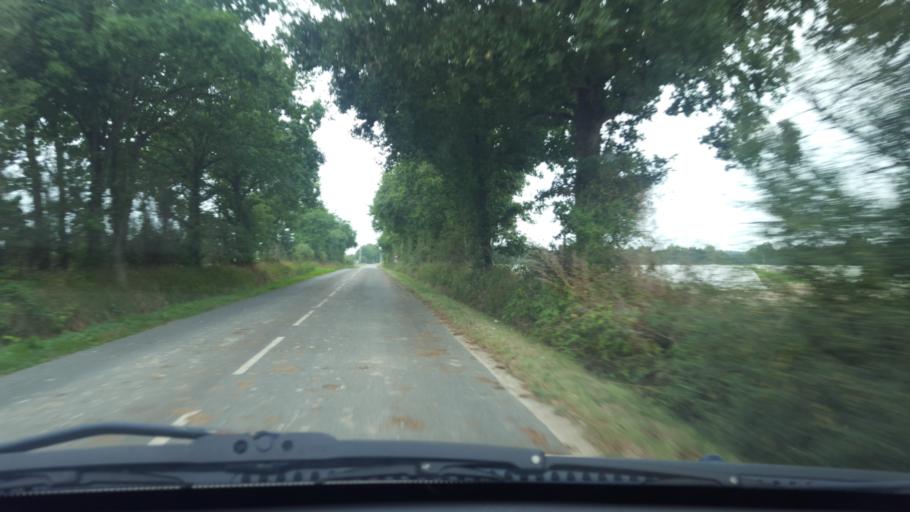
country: FR
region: Pays de la Loire
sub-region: Departement de la Loire-Atlantique
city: Saint-Philbert-de-Grand-Lieu
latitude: 46.9971
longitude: -1.6591
